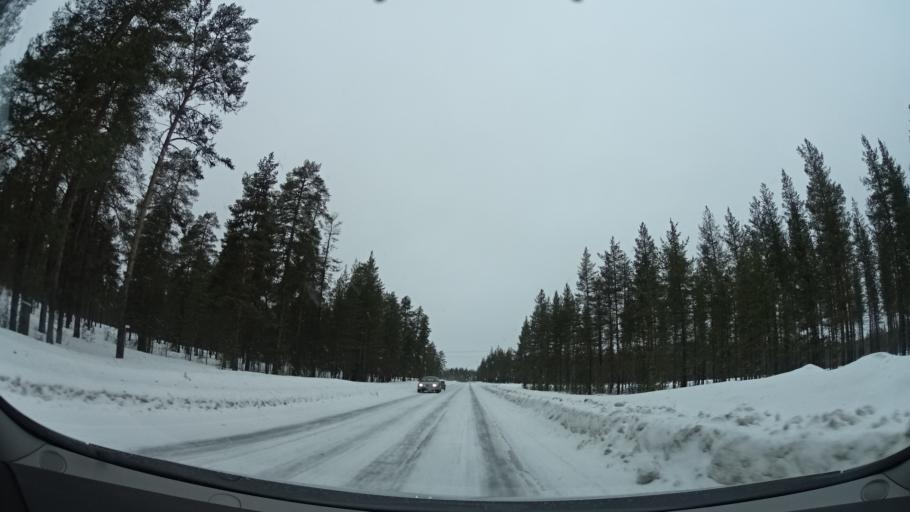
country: SE
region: Vaesterbotten
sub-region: Mala Kommun
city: Mala
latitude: 65.1353
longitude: 18.8650
